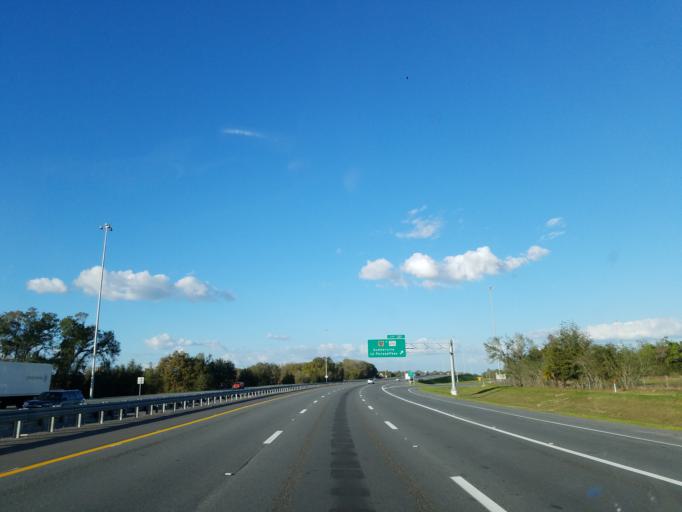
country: US
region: Florida
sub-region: Sumter County
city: Lake Panasoffkee
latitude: 28.7491
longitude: -82.1053
